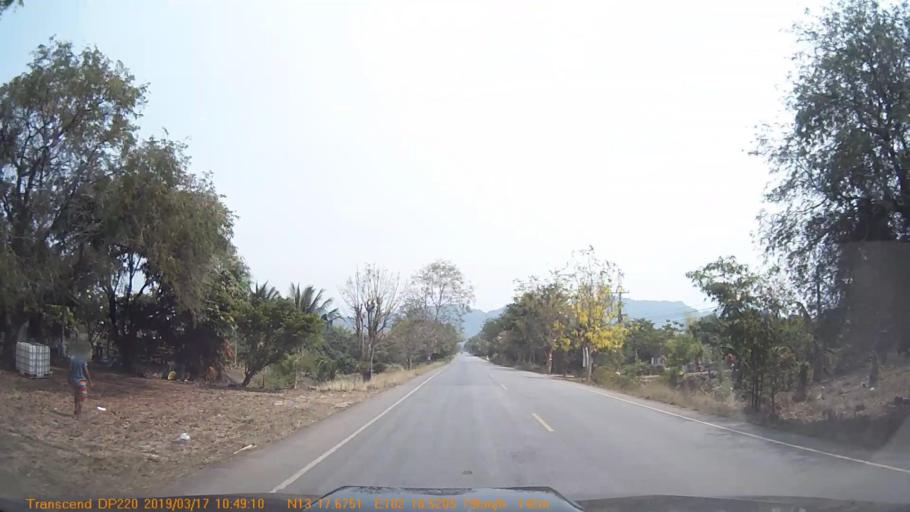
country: TH
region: Sa Kaeo
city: Wang Sombun
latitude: 13.2950
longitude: 102.3091
